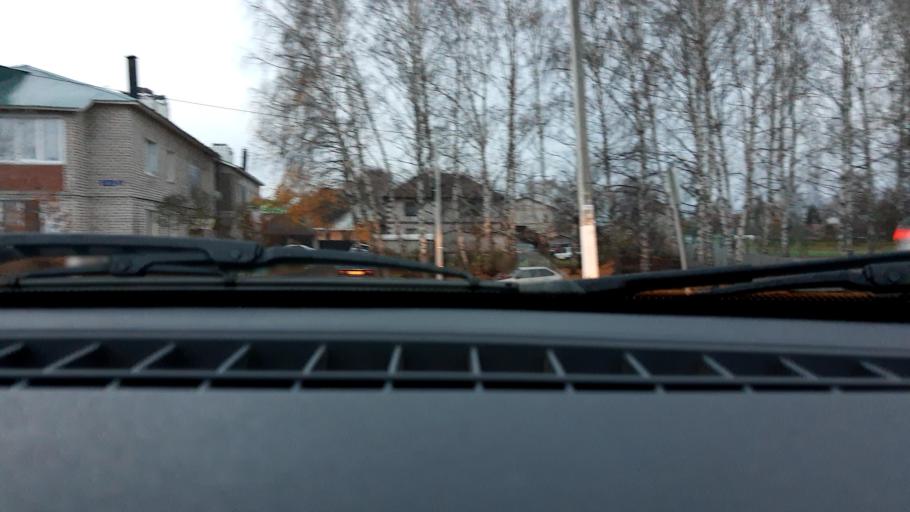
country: RU
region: Bashkortostan
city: Mikhaylovka
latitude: 54.7820
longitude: 55.8372
